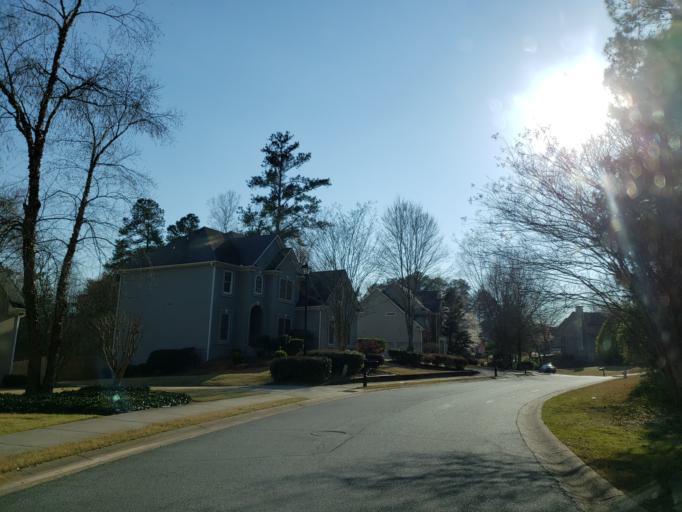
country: US
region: Georgia
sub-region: Cobb County
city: Marietta
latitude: 33.9839
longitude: -84.5127
